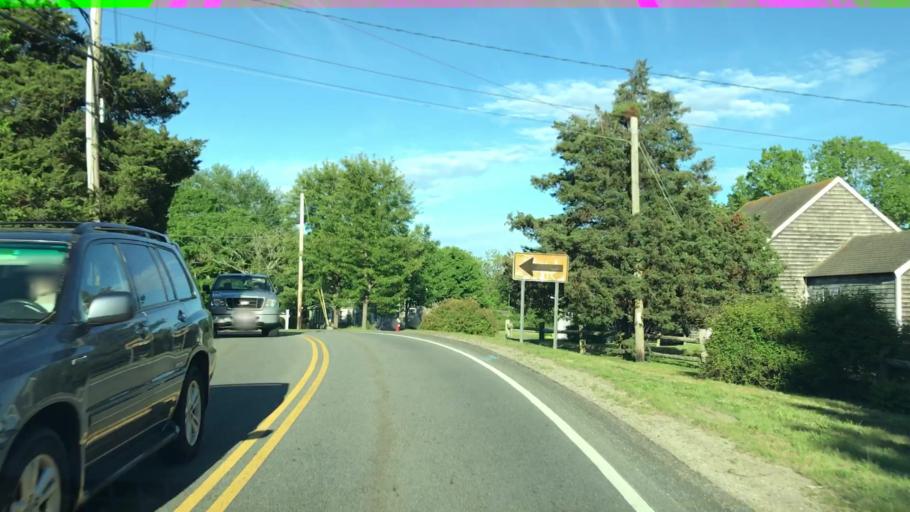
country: US
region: Massachusetts
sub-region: Barnstable County
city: East Harwich
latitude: 41.6997
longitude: -70.0188
